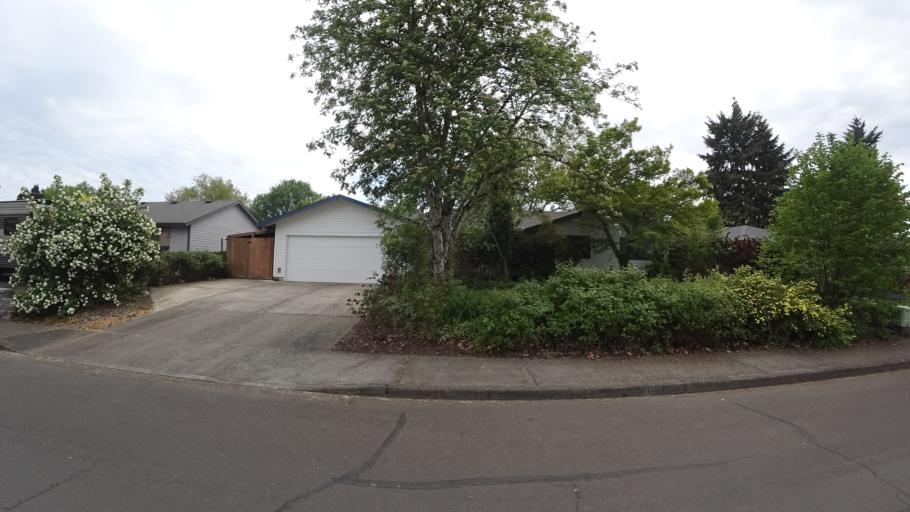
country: US
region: Oregon
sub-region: Washington County
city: Hillsboro
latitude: 45.4967
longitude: -122.9648
